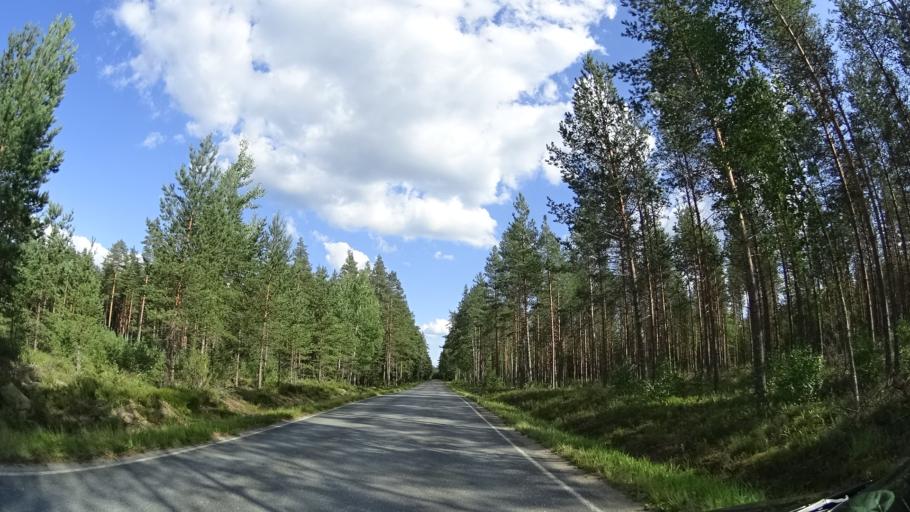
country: FI
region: Uusimaa
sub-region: Helsinki
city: Kaerkoelae
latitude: 60.7438
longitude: 24.0812
